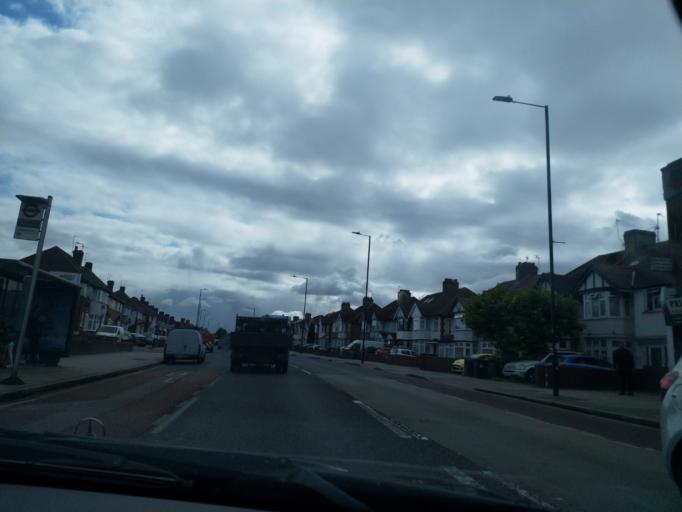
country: GB
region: England
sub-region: Greater London
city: Harrow
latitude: 51.5869
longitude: -0.2993
